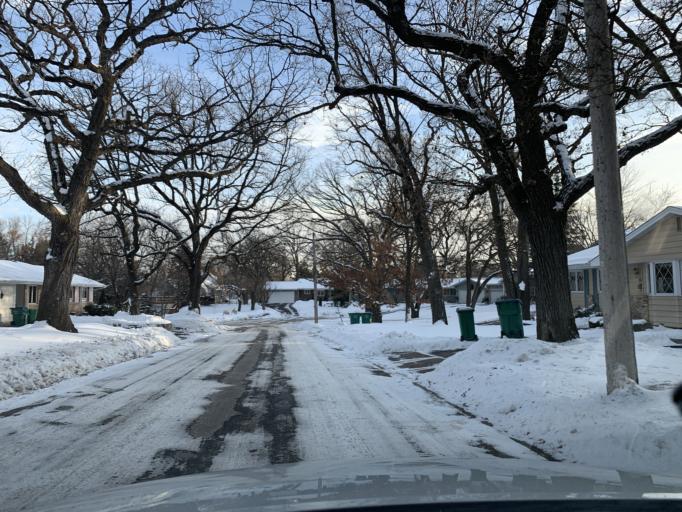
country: US
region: Minnesota
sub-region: Hennepin County
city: Minnetonka Mills
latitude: 44.9461
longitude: -93.3973
